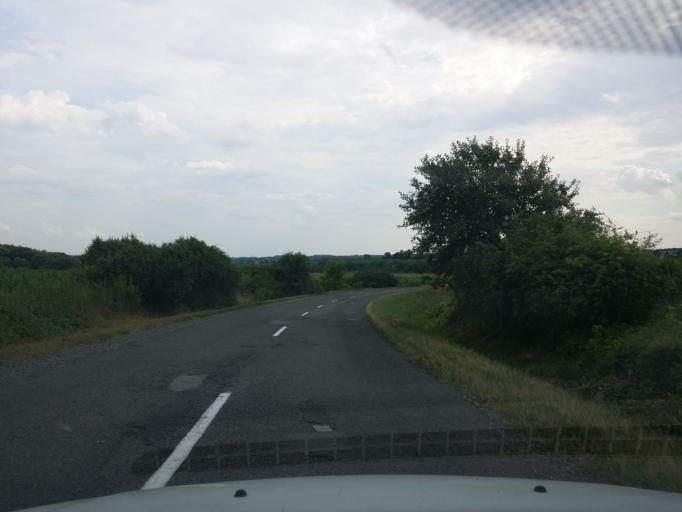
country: HU
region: Nograd
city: Bercel
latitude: 47.9000
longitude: 19.3714
